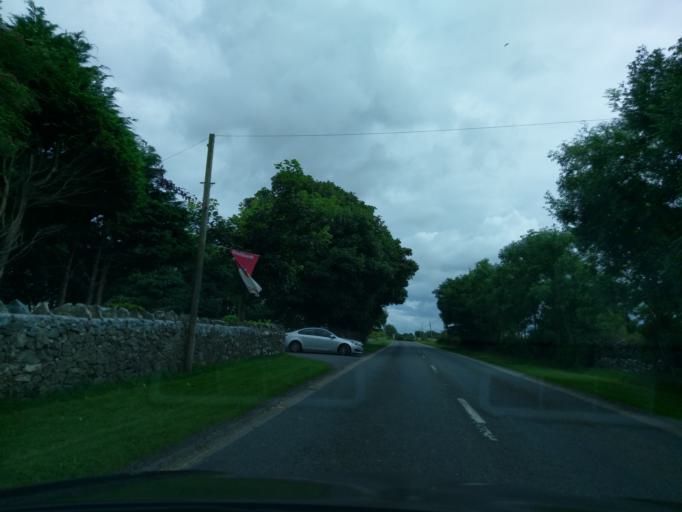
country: IE
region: Connaught
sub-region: County Galway
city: Oranmore
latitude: 53.1911
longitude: -8.8527
